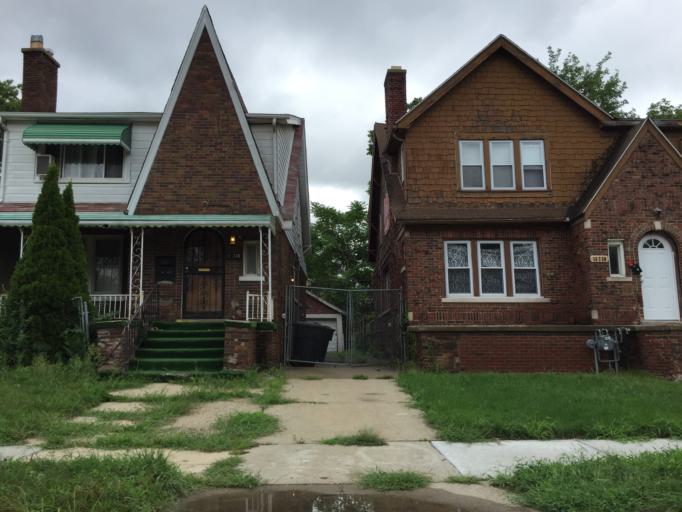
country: US
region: Michigan
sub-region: Oakland County
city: Oak Park
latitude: 42.4117
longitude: -83.1579
